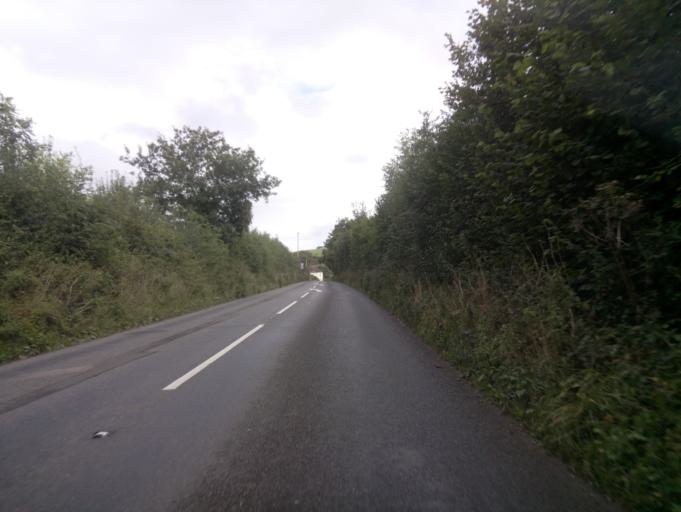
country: GB
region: England
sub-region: Devon
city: Modbury
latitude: 50.3442
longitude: -3.8818
